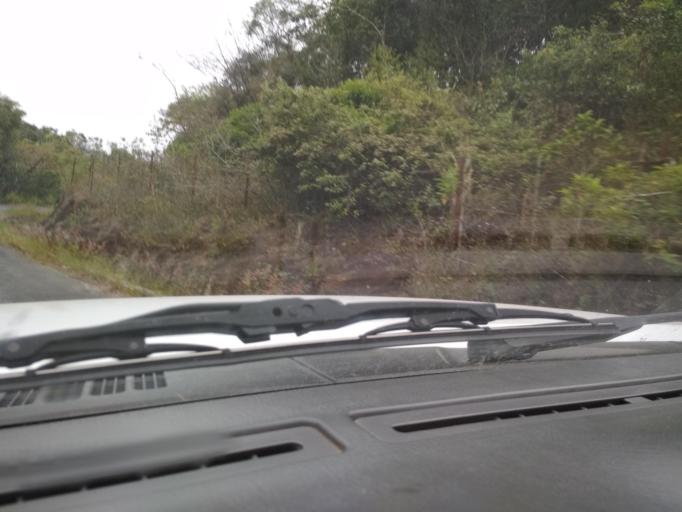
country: MX
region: Veracruz
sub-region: Emiliano Zapata
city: Dos Rios
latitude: 19.5259
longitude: -96.7977
